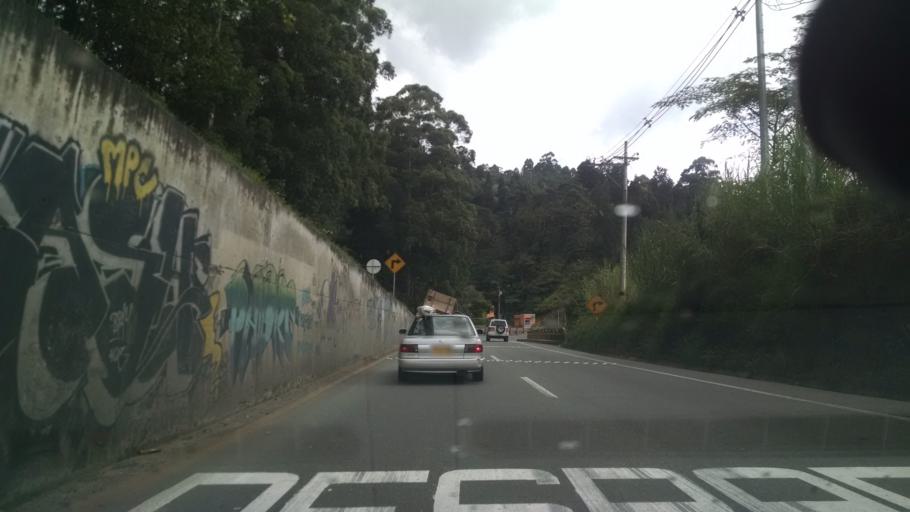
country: CO
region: Antioquia
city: Caldas
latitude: 6.1120
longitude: -75.6335
